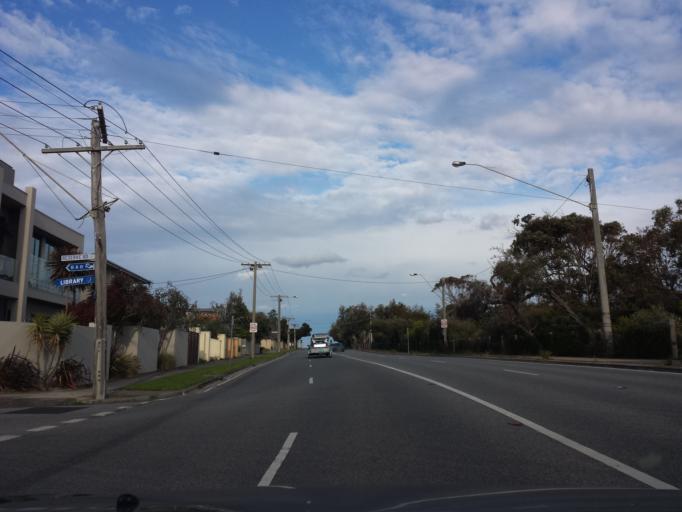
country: AU
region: Victoria
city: Beaumaris
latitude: -37.9930
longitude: 145.0315
